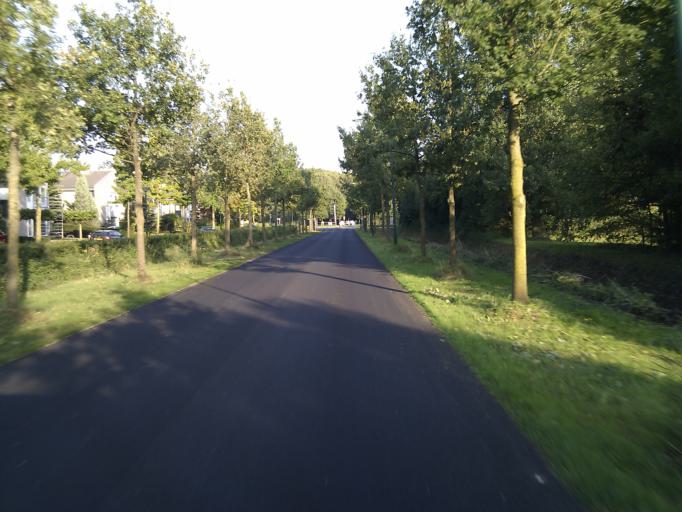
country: NL
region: North Brabant
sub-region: Gemeente Sint-Oedenrode
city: Sint-Oedenrode
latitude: 51.5560
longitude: 5.4517
